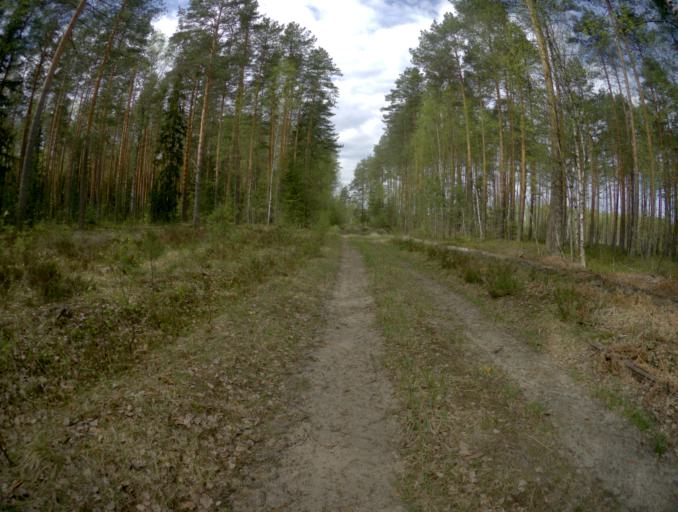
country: RU
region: Vladimir
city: Golovino
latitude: 55.9301
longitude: 40.3666
